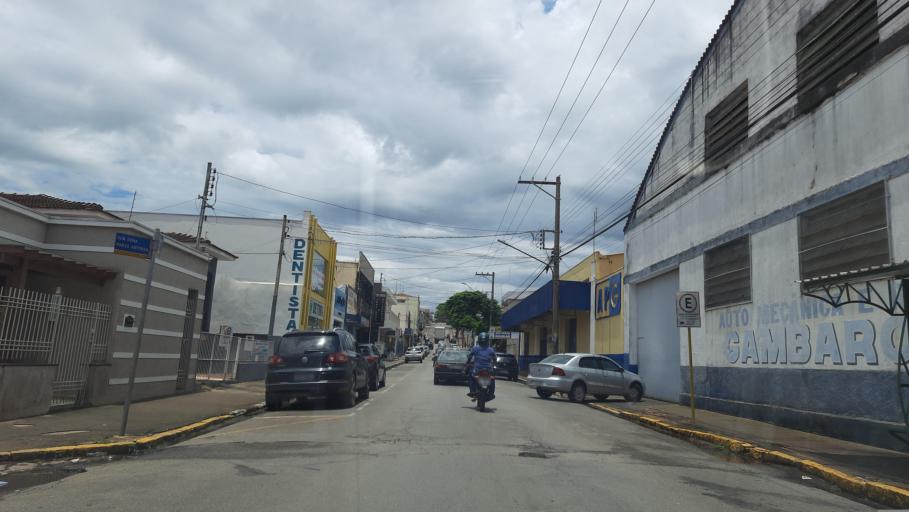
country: BR
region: Sao Paulo
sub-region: Vargem Grande Do Sul
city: Vargem Grande do Sul
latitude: -21.8353
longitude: -46.8959
